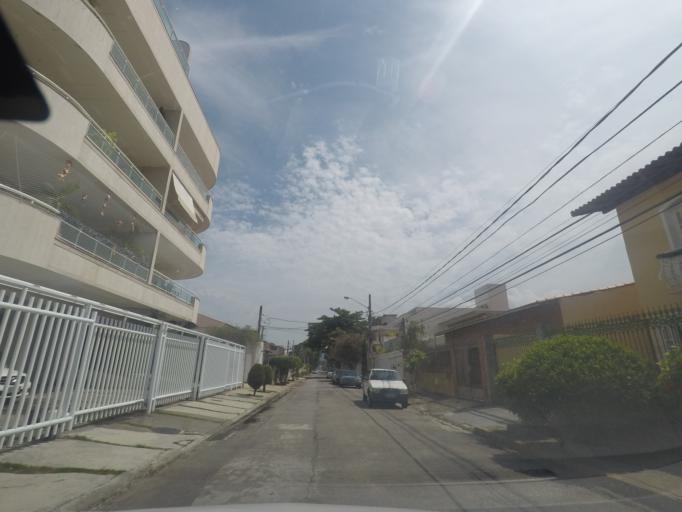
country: BR
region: Rio de Janeiro
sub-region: Rio De Janeiro
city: Rio de Janeiro
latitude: -22.8116
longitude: -43.2112
